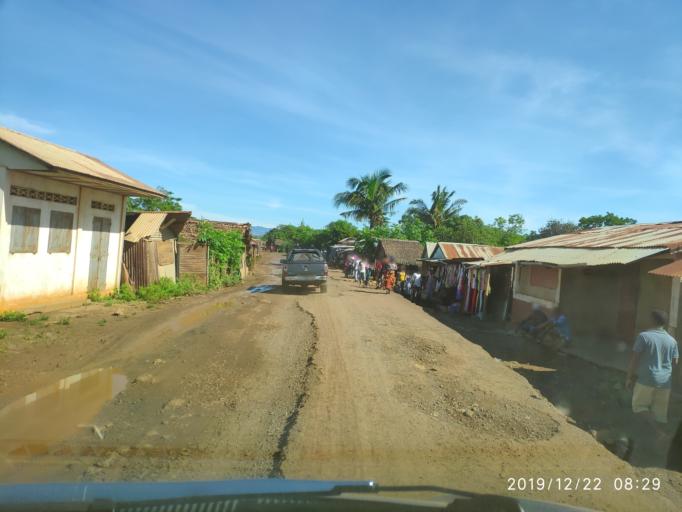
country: MG
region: Diana
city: Sadjoavato
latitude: -12.8981
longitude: 49.2122
